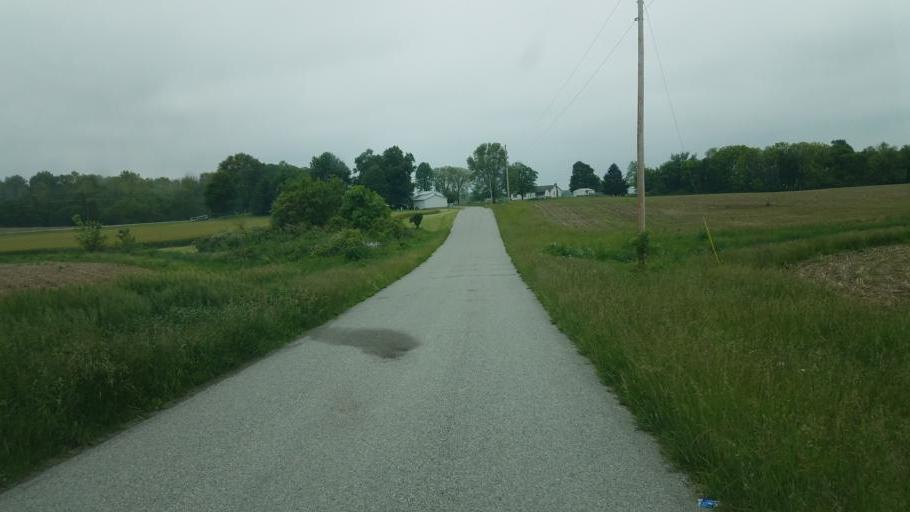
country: US
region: Ohio
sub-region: Knox County
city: Centerburg
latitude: 40.3761
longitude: -82.7366
